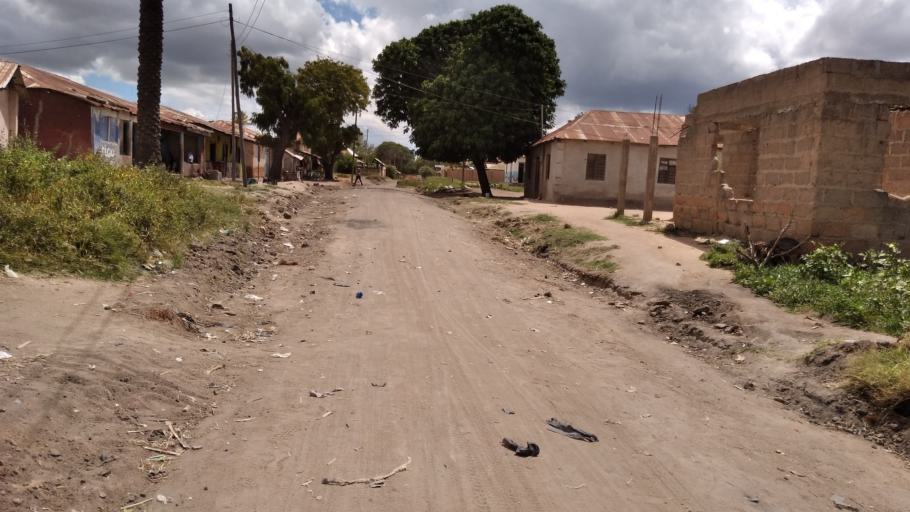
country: TZ
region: Dodoma
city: Dodoma
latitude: -6.1640
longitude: 35.7411
